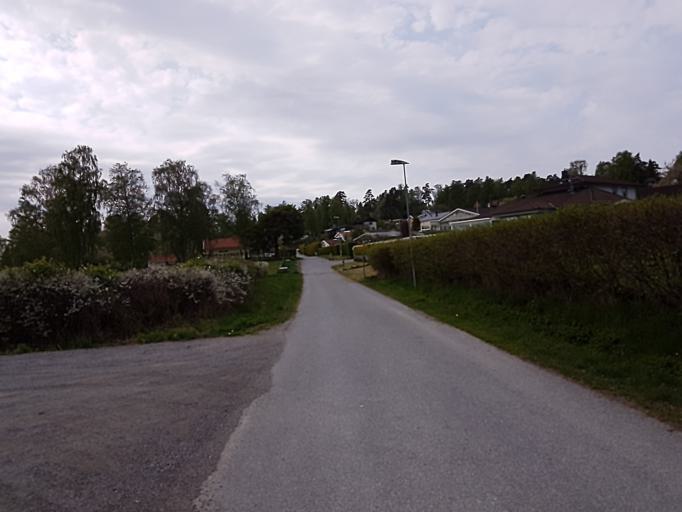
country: SE
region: Stockholm
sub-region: Salems Kommun
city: Ronninge
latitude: 59.2726
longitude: 17.7392
